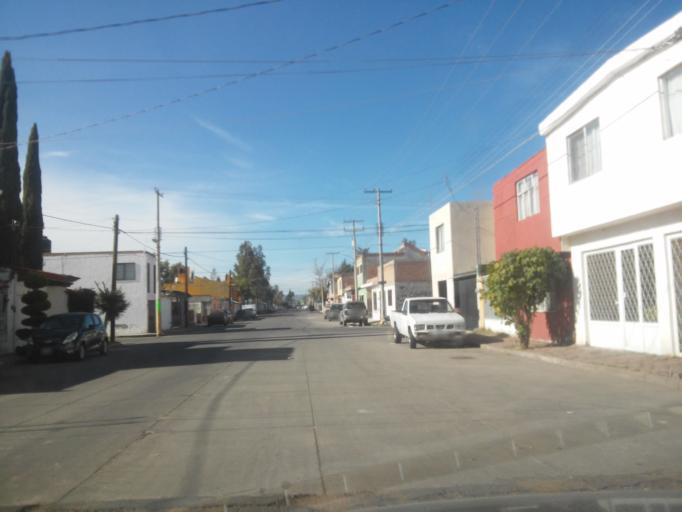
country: MX
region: Durango
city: Victoria de Durango
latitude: 24.0435
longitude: -104.6533
